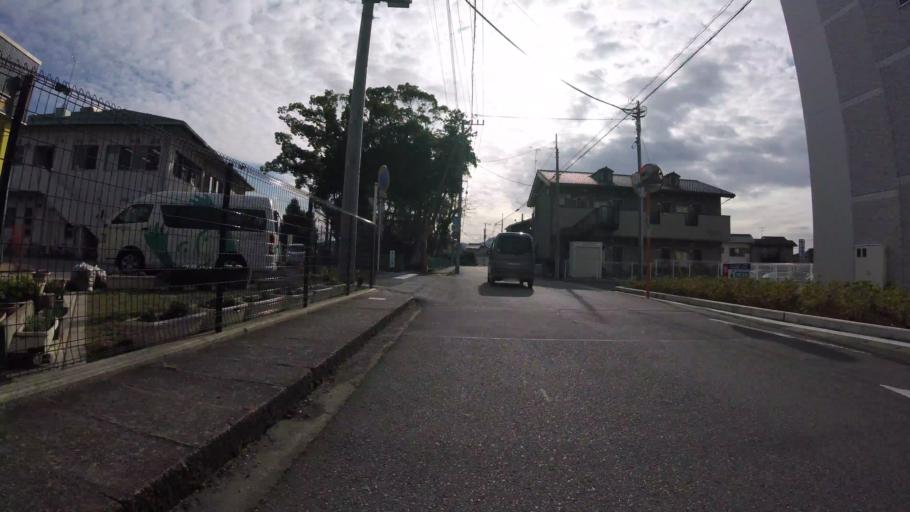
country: JP
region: Shizuoka
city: Mishima
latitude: 35.1068
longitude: 138.9175
